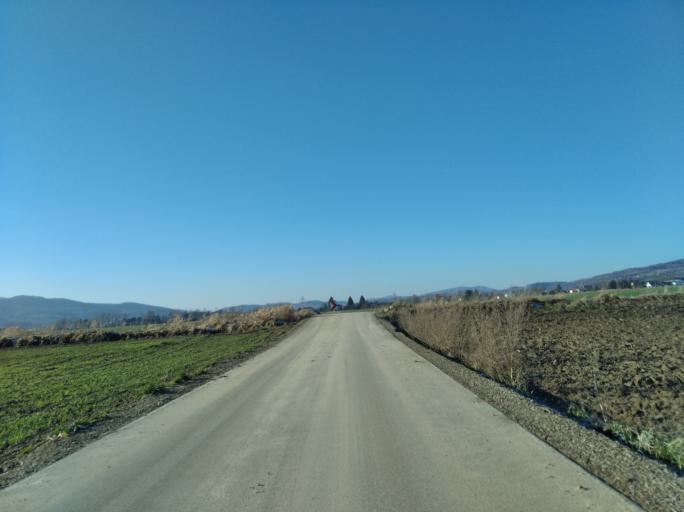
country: PL
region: Subcarpathian Voivodeship
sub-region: Powiat strzyzowski
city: Wisniowa
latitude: 49.8671
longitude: 21.6957
